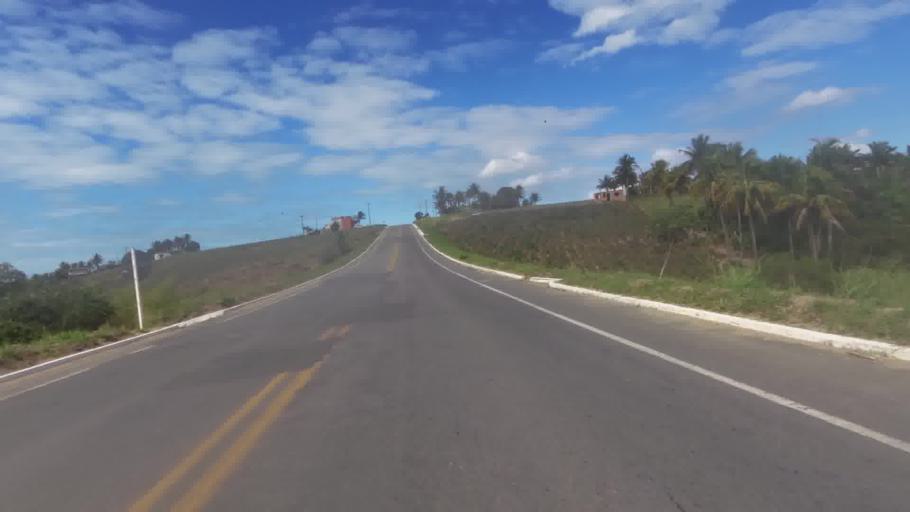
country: BR
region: Espirito Santo
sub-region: Marataizes
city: Marataizes
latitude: -21.0589
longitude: -40.8491
